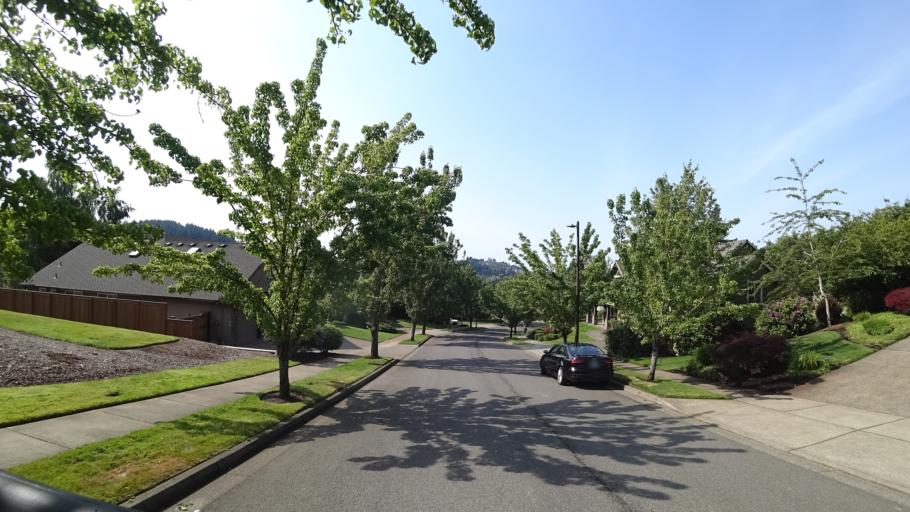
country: US
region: Oregon
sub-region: Clackamas County
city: Happy Valley
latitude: 45.4555
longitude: -122.5215
